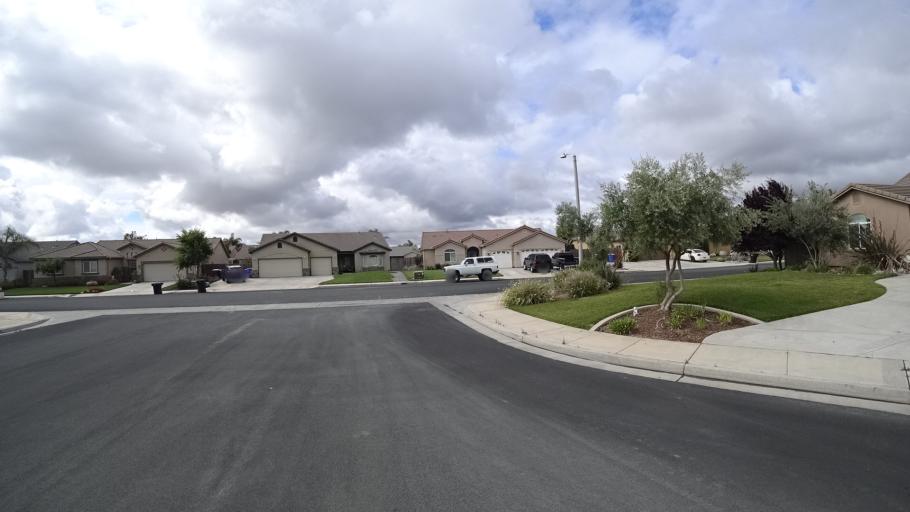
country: US
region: California
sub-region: Kings County
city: Lucerne
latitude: 36.3495
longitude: -119.6701
